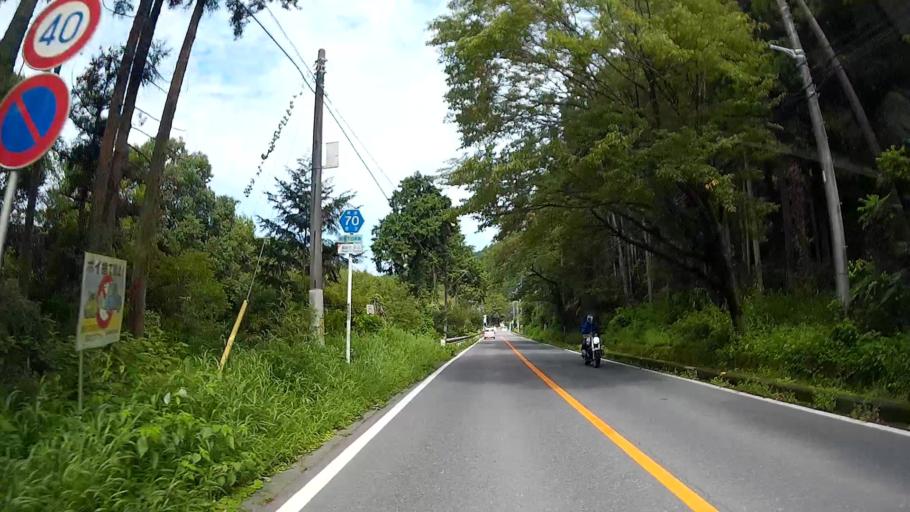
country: JP
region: Saitama
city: Hanno
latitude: 35.8668
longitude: 139.2840
